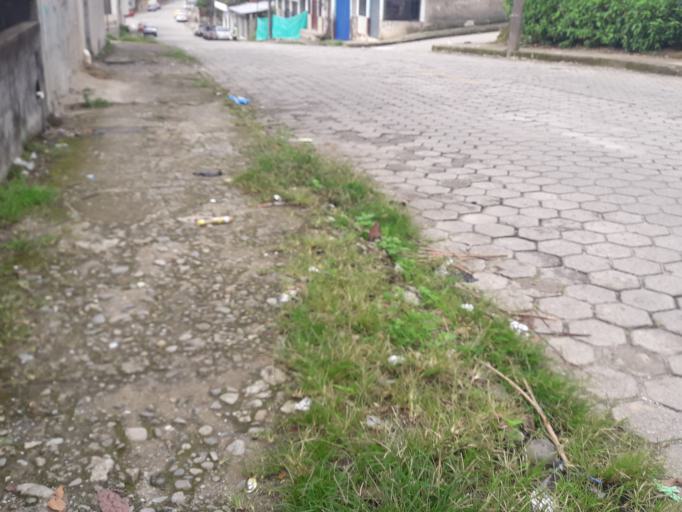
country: EC
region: Napo
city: Tena
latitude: -0.9977
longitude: -77.8148
